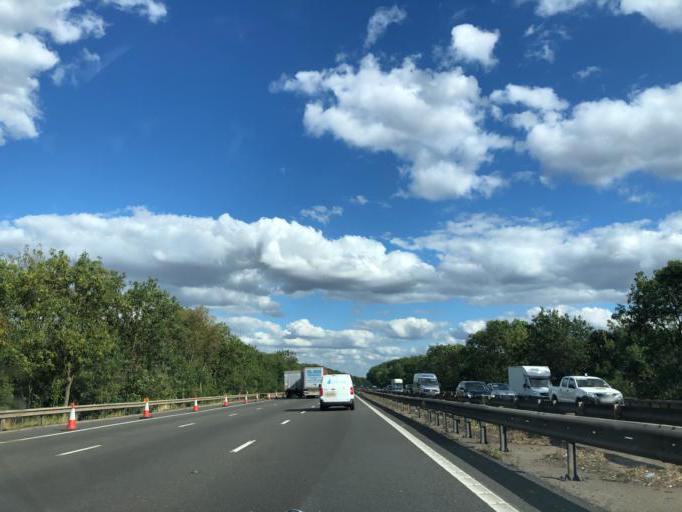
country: GB
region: England
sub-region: Milton Keynes
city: Gayhurst
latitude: 52.1047
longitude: -0.7763
